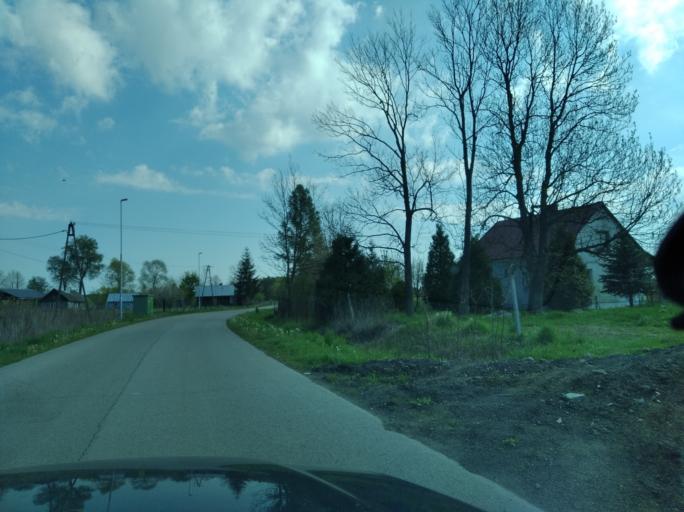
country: PL
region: Subcarpathian Voivodeship
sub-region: Powiat lubaczowski
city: Wielkie Oczy
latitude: 49.9748
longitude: 23.0611
